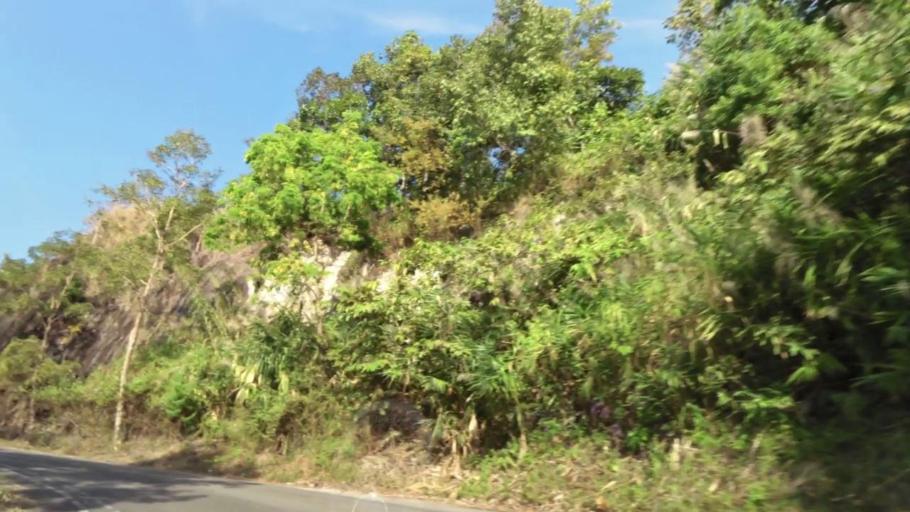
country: TH
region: Chiang Rai
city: Khun Tan
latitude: 19.8790
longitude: 100.3096
